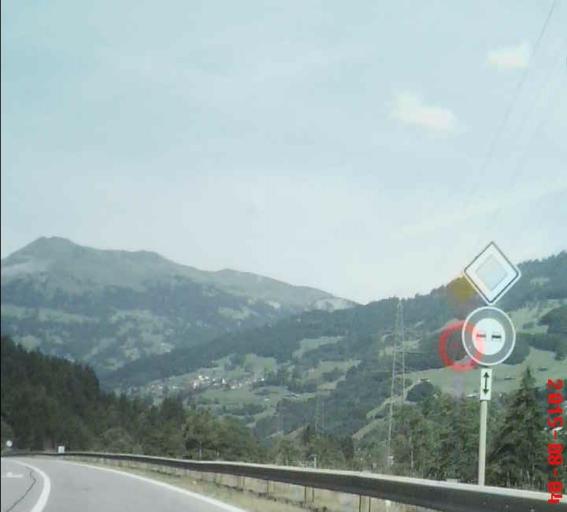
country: CH
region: Grisons
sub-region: Praettigau/Davos District
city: Schiers
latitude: 46.9565
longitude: 9.7049
